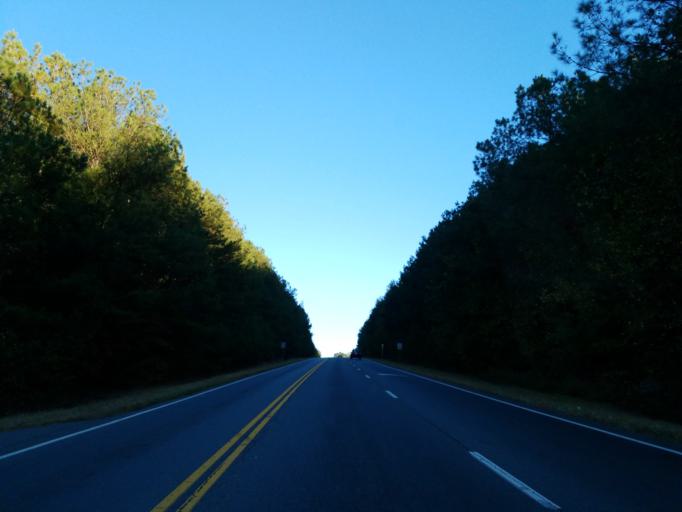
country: US
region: Georgia
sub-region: Dawson County
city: Dawsonville
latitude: 34.3801
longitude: -84.0576
